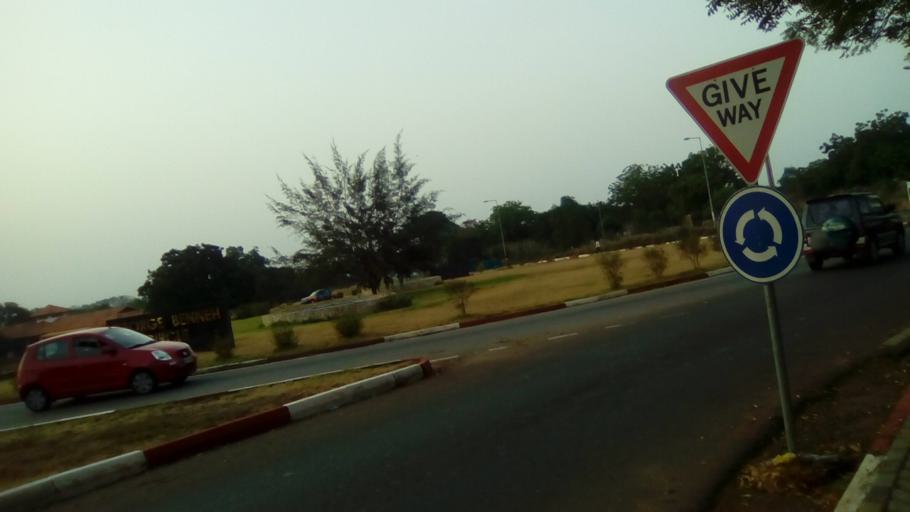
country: GH
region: Greater Accra
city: Medina Estates
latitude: 5.6404
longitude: -0.1838
